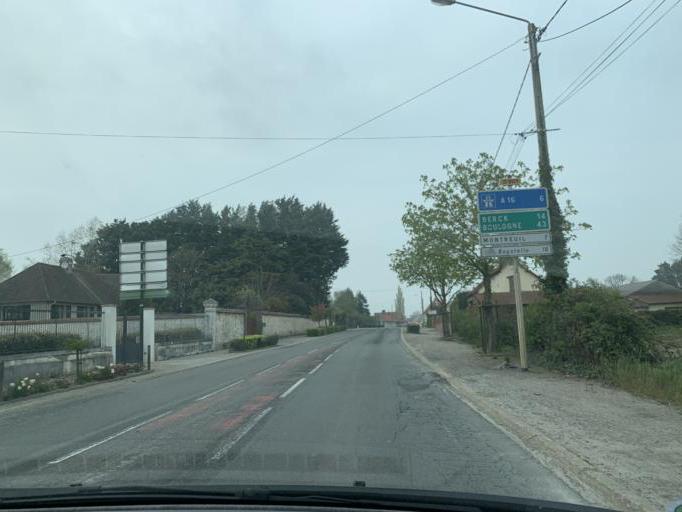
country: FR
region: Nord-Pas-de-Calais
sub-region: Departement du Pas-de-Calais
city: Montreuil
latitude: 50.4056
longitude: 1.7251
